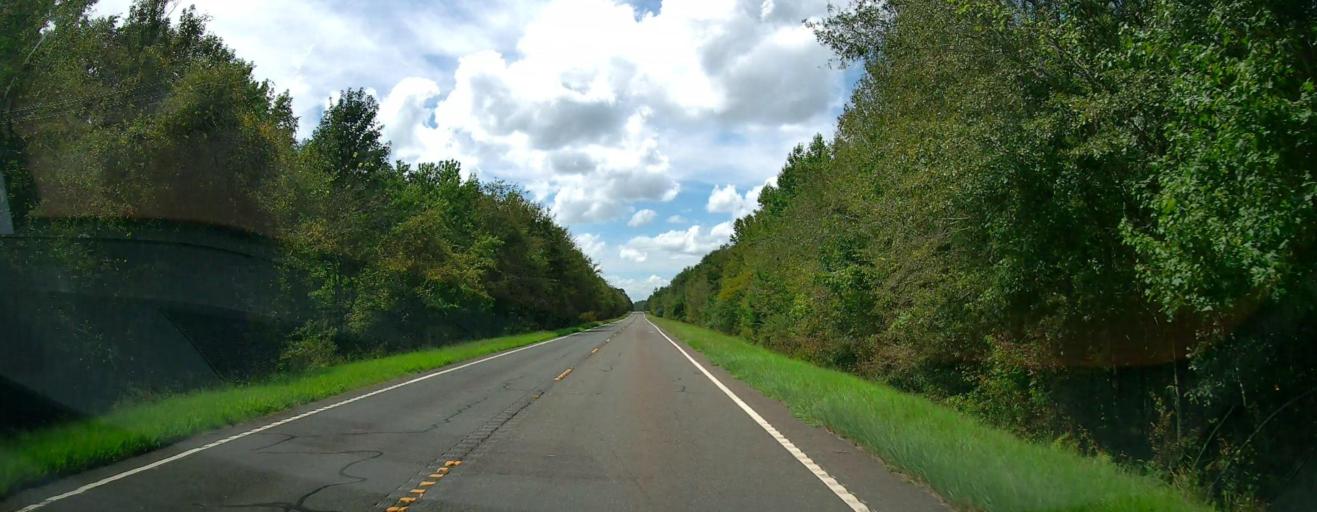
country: US
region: Georgia
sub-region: Macon County
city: Marshallville
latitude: 32.4331
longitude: -84.0280
